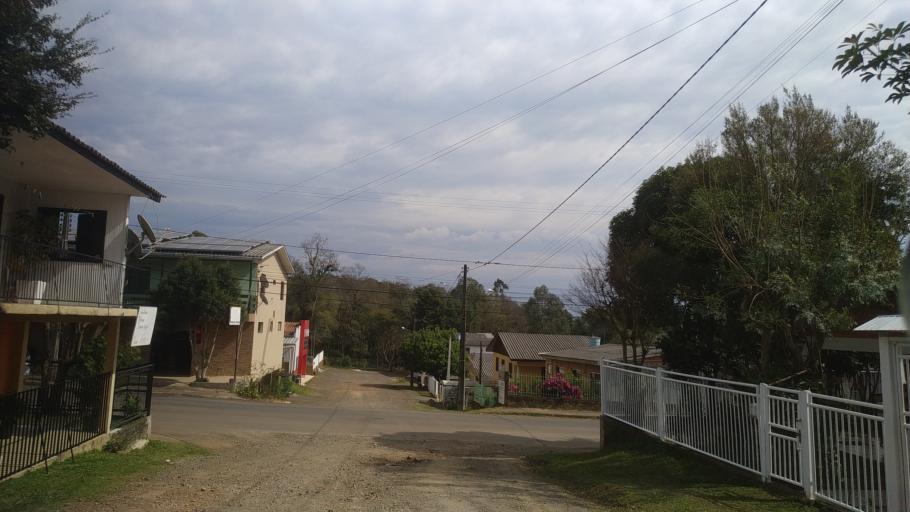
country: BR
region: Santa Catarina
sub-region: Chapeco
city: Chapeco
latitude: -27.1332
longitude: -52.6191
